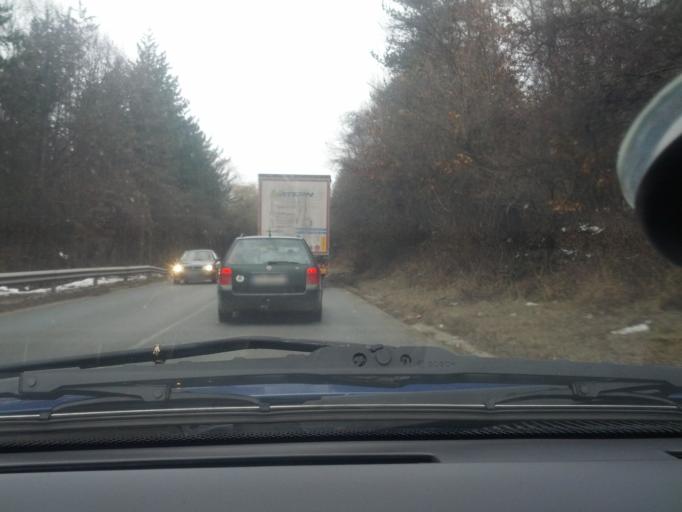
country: BG
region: Vratsa
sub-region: Obshtina Mezdra
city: Mezdra
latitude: 43.0126
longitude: 23.6944
